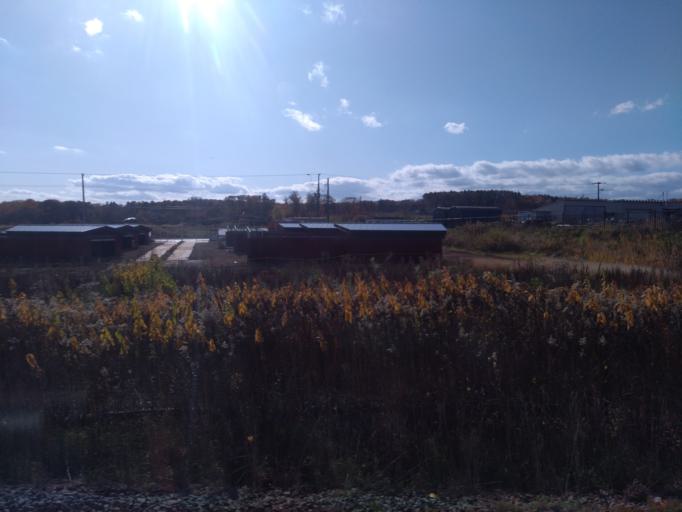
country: JP
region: Hokkaido
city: Kitahiroshima
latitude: 42.9926
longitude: 141.5535
